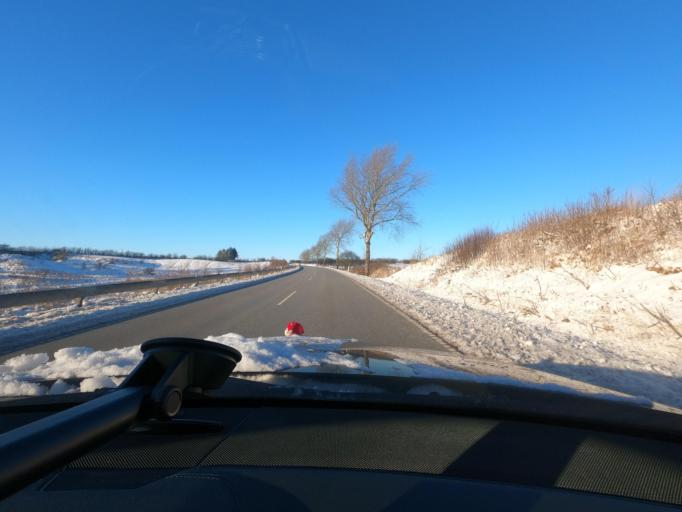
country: DK
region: South Denmark
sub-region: Aabenraa Kommune
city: Rodekro
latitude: 55.0843
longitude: 9.2165
